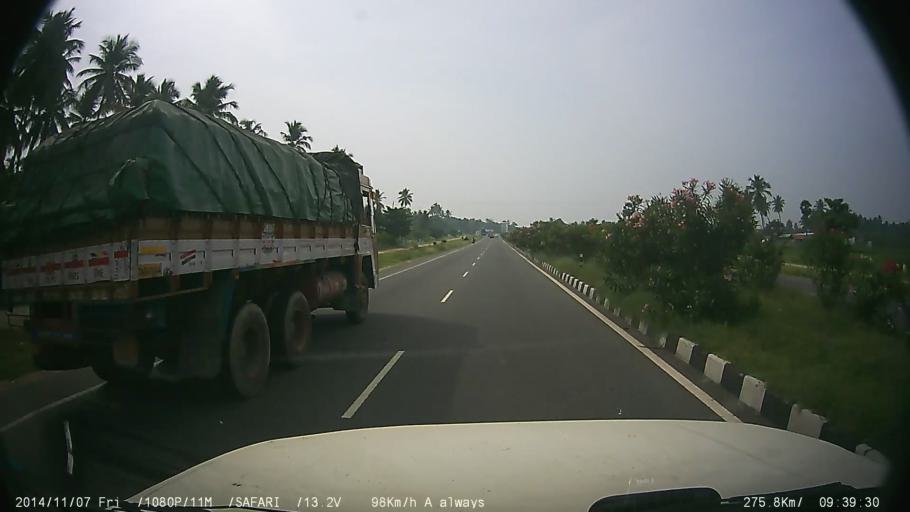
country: IN
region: Tamil Nadu
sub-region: Erode
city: Perundurai
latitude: 11.3344
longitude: 77.6298
